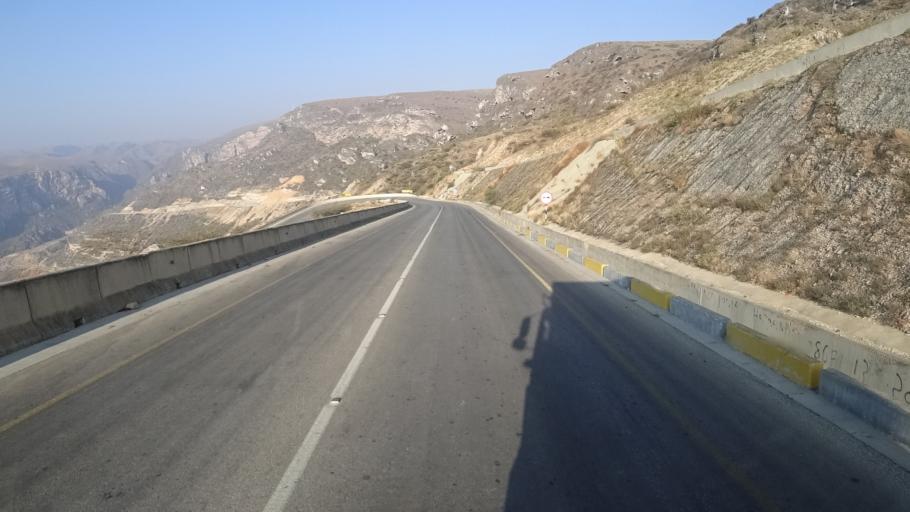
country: YE
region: Al Mahrah
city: Hawf
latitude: 16.7558
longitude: 53.2334
